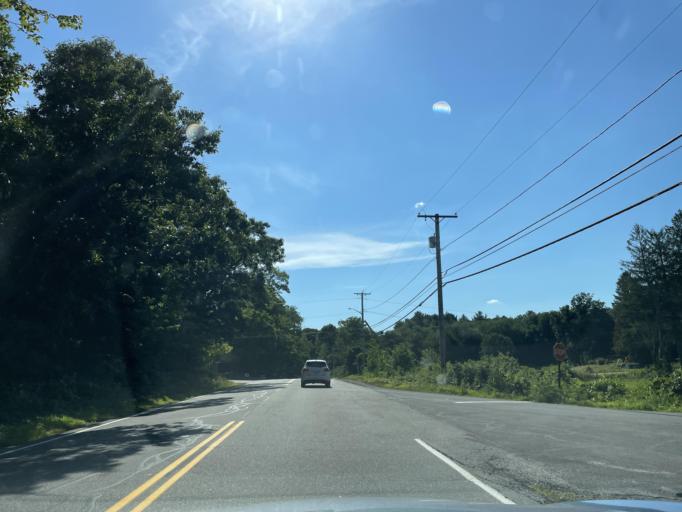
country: US
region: Massachusetts
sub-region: Worcester County
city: Sutton
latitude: 42.1515
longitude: -71.7090
